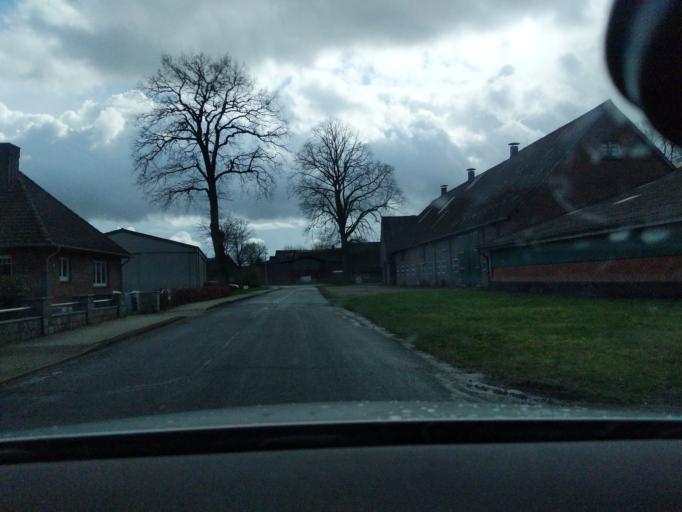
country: DE
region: Lower Saxony
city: Kranenburg
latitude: 53.6096
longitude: 9.2018
